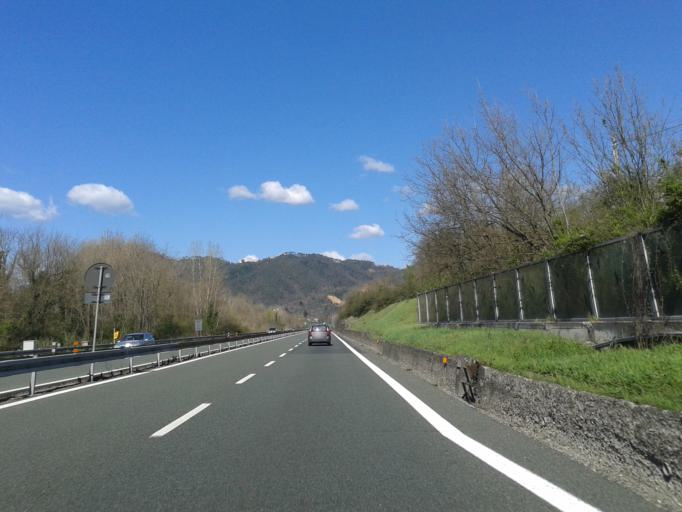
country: IT
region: Liguria
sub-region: Provincia di La Spezia
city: Beverino
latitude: 44.1995
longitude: 9.8098
